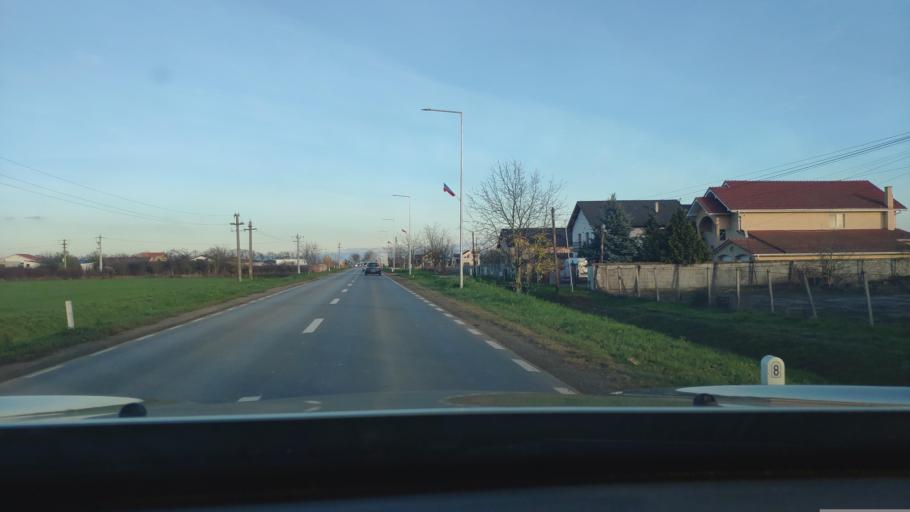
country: RO
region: Satu Mare
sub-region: Comuna Paulesti
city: Paulesti
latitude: 47.7969
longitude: 22.9366
